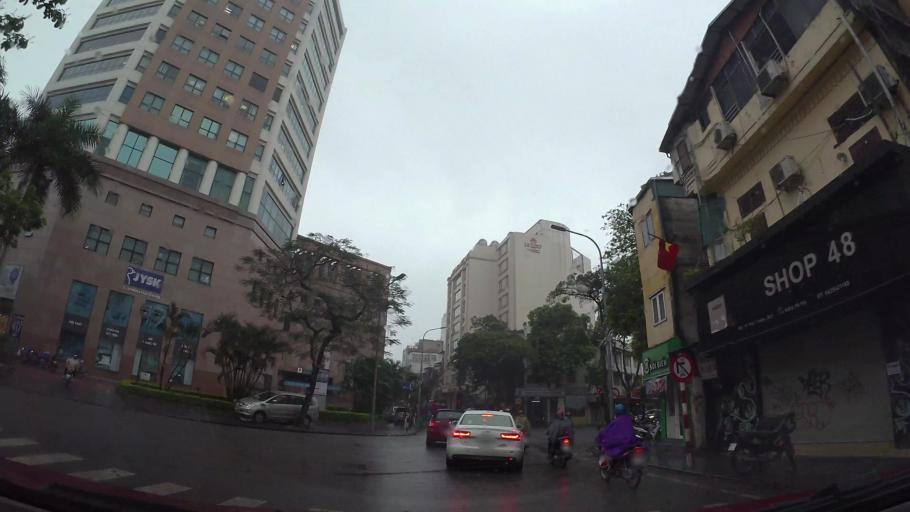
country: VN
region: Ha Noi
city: Hanoi
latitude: 21.0260
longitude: 105.8453
